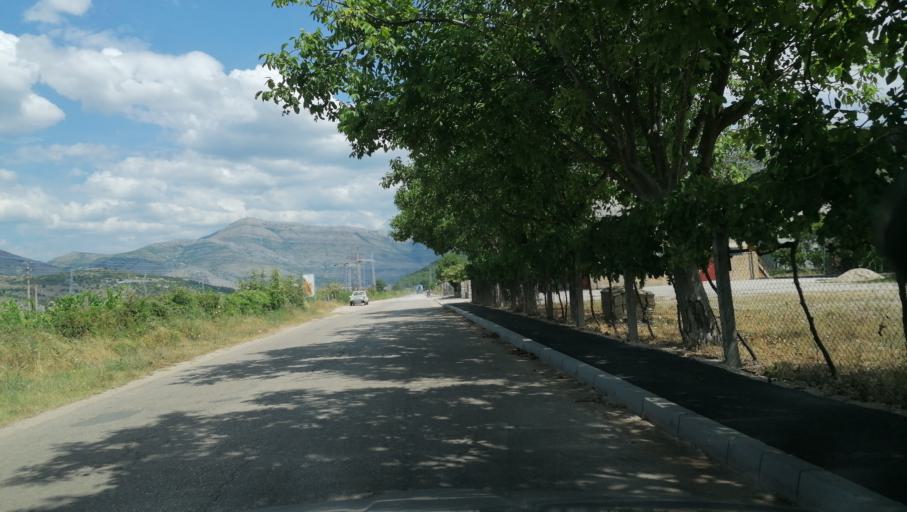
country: BA
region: Republika Srpska
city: Trebinje
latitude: 42.6740
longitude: 18.3300
